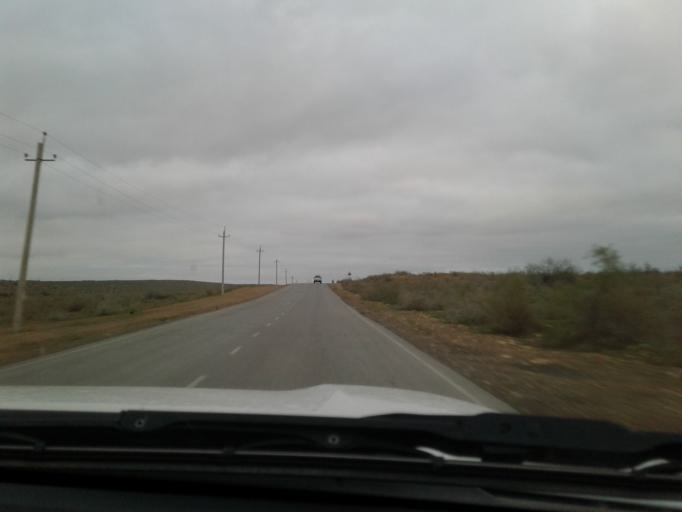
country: TM
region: Lebap
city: Farap
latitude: 39.1067
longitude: 63.7171
